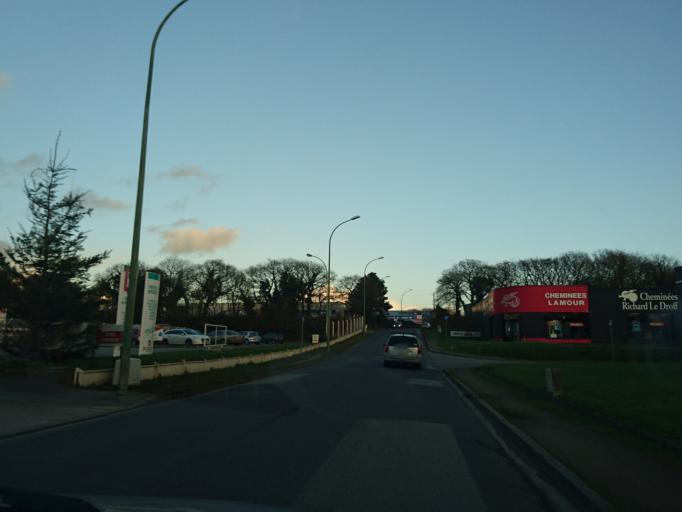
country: FR
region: Brittany
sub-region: Departement du Finistere
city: Gouesnou
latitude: 48.4320
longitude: -4.4562
